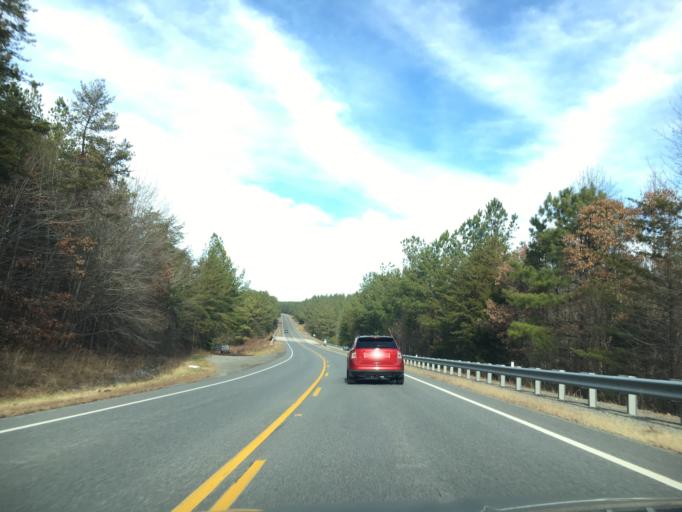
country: US
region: Virginia
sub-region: Louisa County
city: Louisa
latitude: 38.0634
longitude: -77.8793
